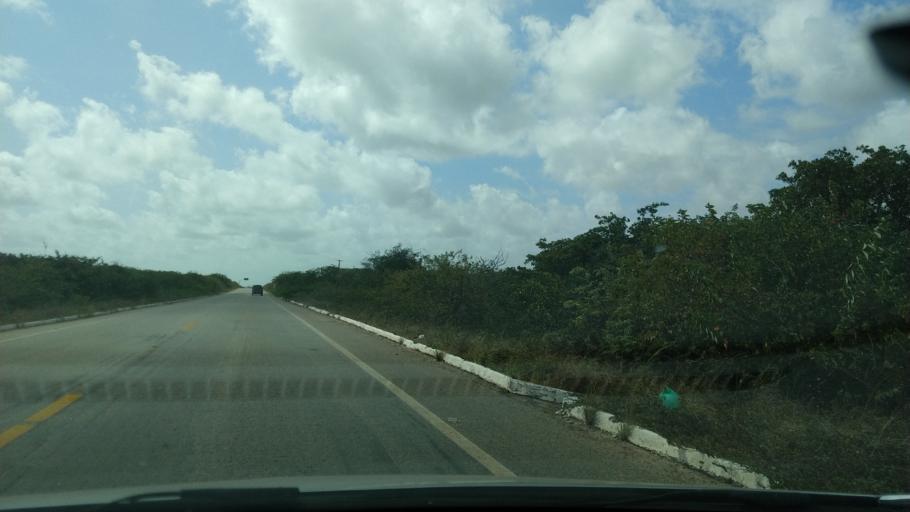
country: BR
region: Rio Grande do Norte
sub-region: Touros
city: Touros
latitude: -5.1934
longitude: -35.5057
